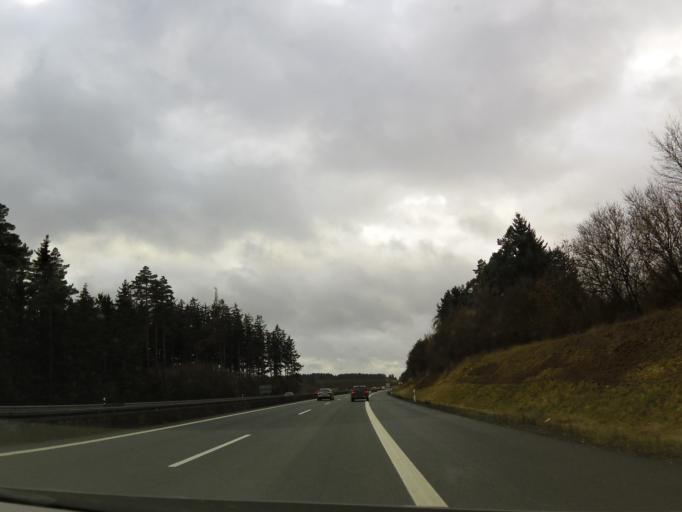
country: DE
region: Bavaria
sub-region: Upper Franconia
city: Schonwald
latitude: 50.2031
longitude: 12.1073
